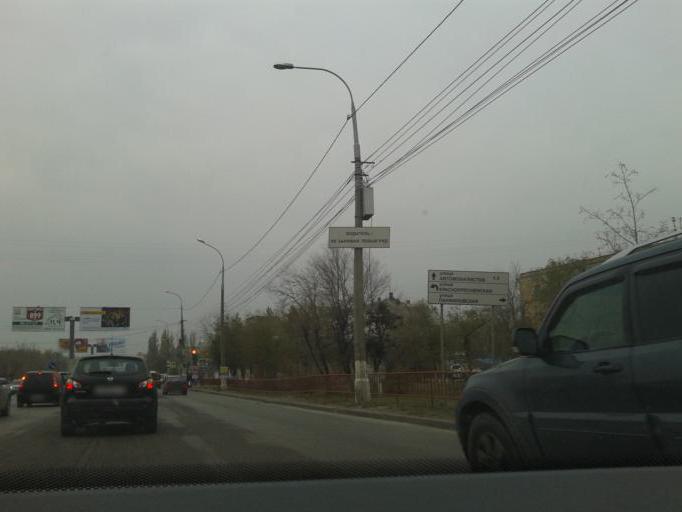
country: RU
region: Volgograd
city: Volgograd
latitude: 48.6601
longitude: 44.4385
